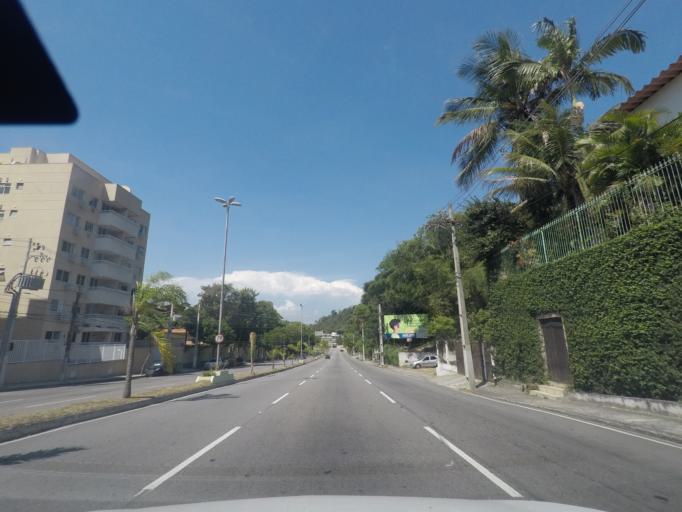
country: BR
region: Rio de Janeiro
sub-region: Niteroi
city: Niteroi
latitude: -22.9186
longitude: -43.0512
